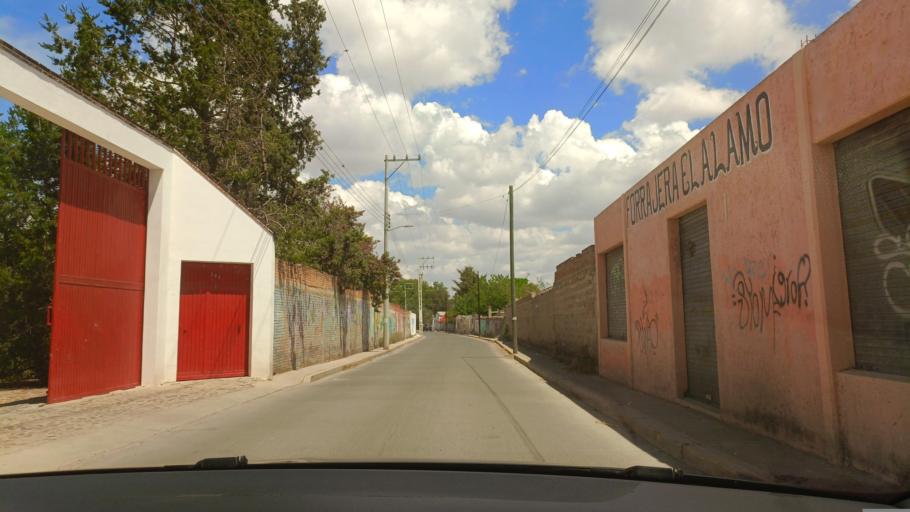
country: MX
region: Guanajuato
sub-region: San Luis de la Paz
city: San Luis de la Paz
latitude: 21.3042
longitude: -100.5203
